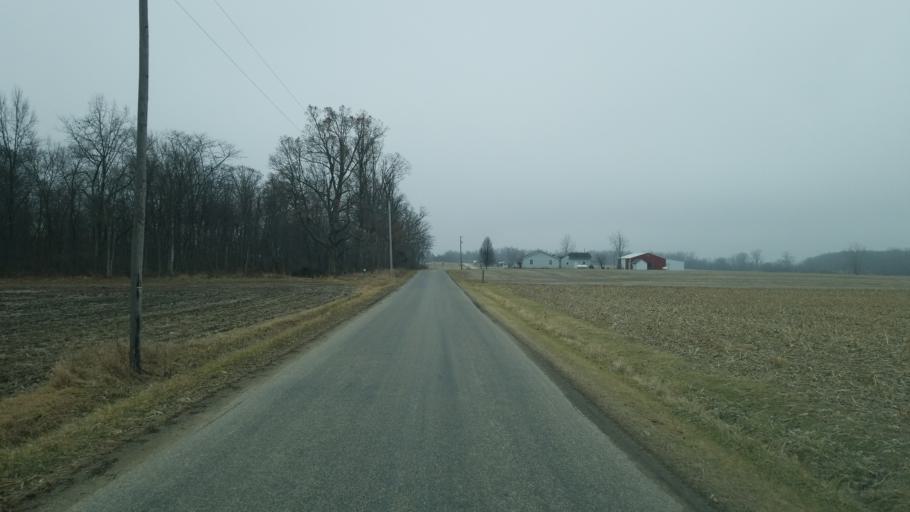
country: US
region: Indiana
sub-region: Adams County
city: Geneva
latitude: 40.5711
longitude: -85.0400
